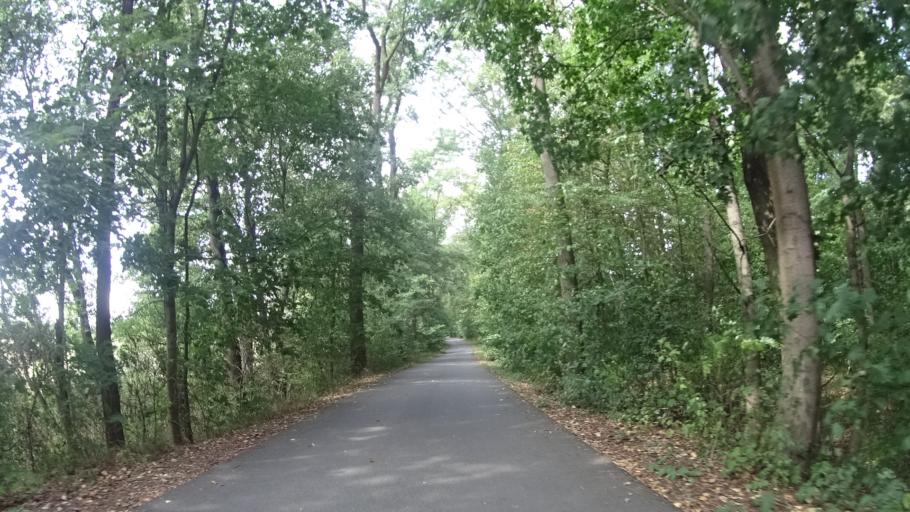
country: CZ
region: Olomoucky
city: Horka nad Moravou
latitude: 49.6494
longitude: 17.1956
